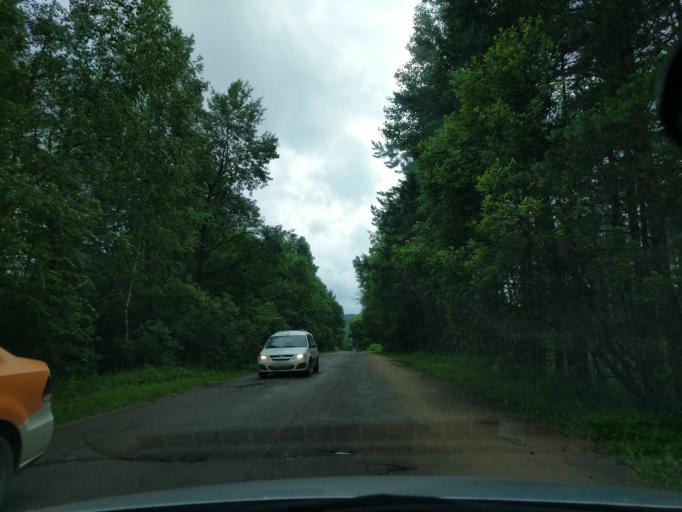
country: RU
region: Kaluga
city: Nikola-Lenivets
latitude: 54.7717
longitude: 35.7143
